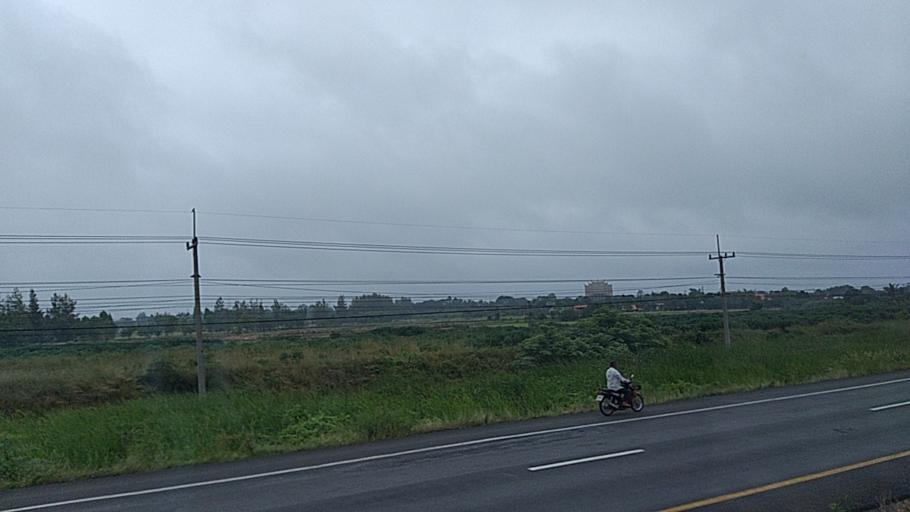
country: TH
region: Nakhon Ratchasima
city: Phimai
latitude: 15.3084
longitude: 102.4256
